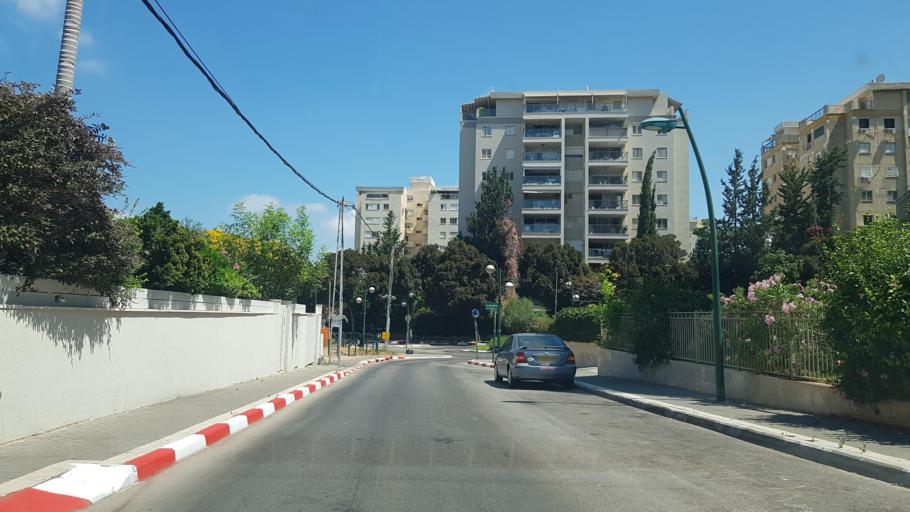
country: IL
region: Tel Aviv
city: Ramat HaSharon
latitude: 32.1520
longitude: 34.8394
